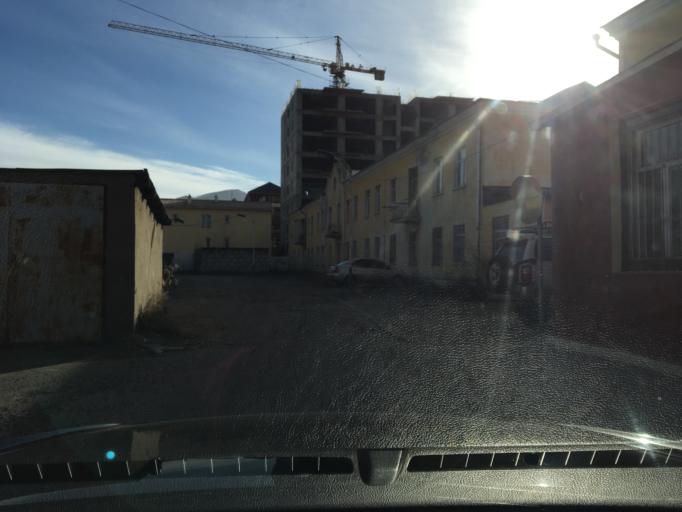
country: MN
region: Ulaanbaatar
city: Ulaanbaatar
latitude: 47.8945
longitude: 106.9174
